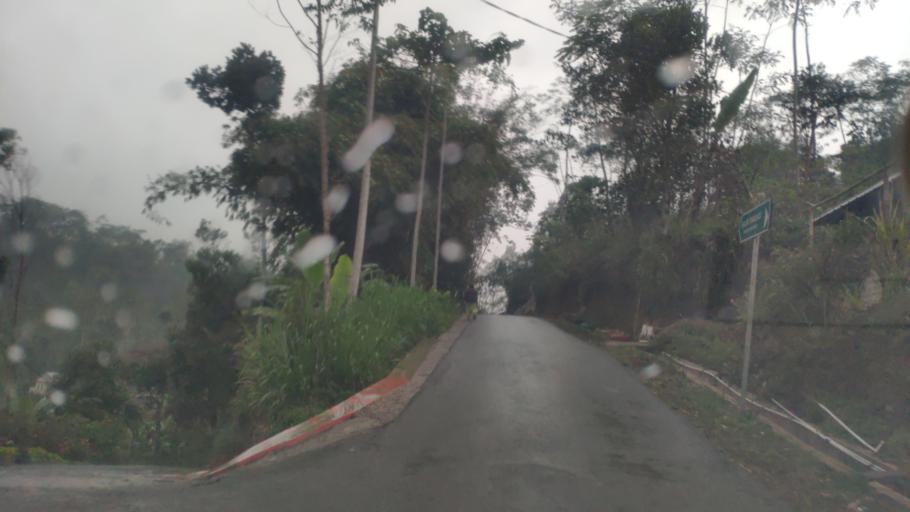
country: ID
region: Central Java
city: Wonosobo
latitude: -7.2763
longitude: 109.7334
